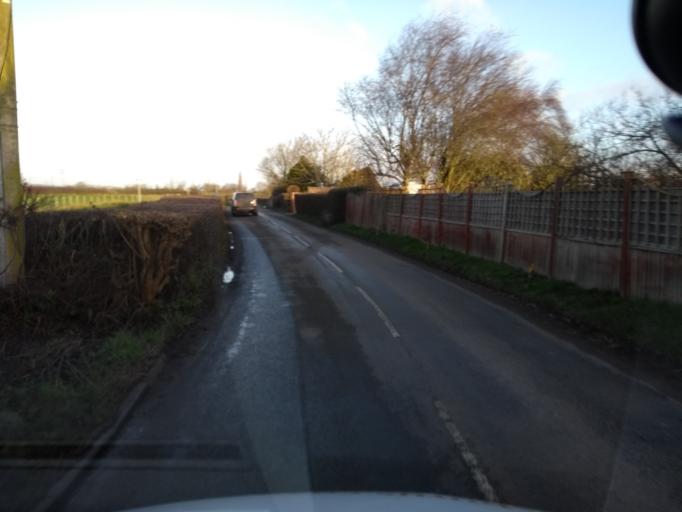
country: GB
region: England
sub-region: Somerset
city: Bridgwater
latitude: 51.1430
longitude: -3.0046
